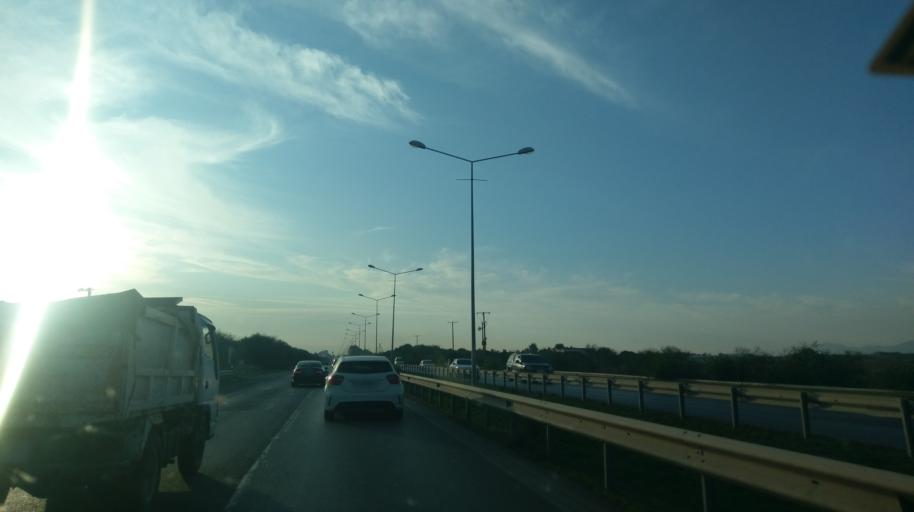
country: CY
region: Lefkosia
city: Nicosia
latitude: 35.2152
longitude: 33.4021
